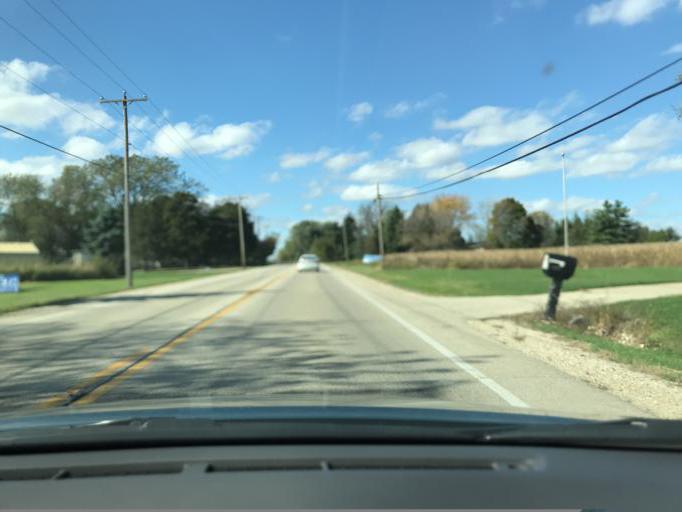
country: US
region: Wisconsin
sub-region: Kenosha County
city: Somers
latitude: 42.6091
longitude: -87.9354
